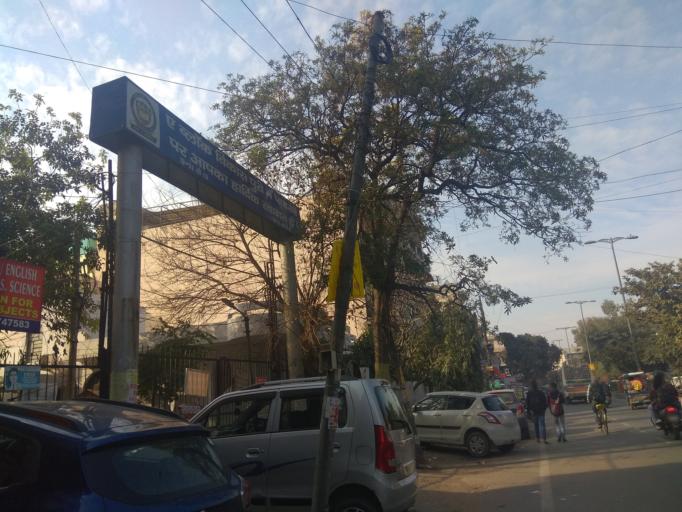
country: IN
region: NCT
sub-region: West Delhi
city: Nangloi Jat
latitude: 28.6273
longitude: 77.0698
